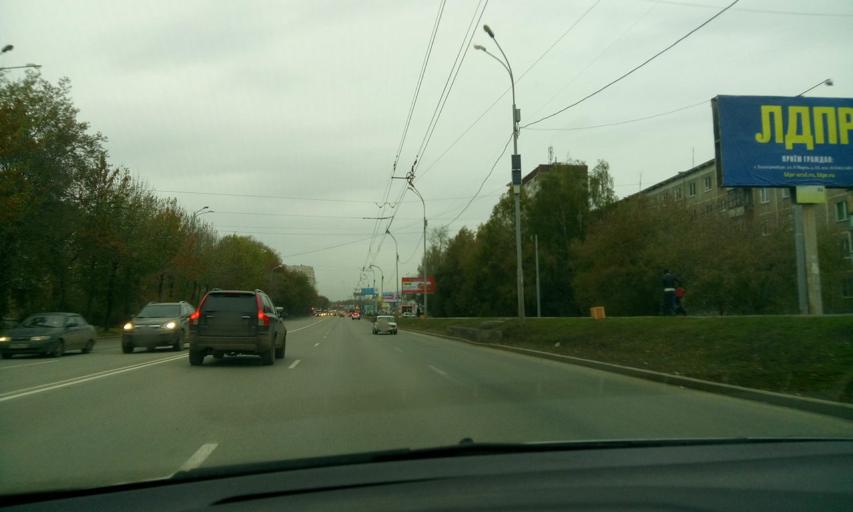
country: RU
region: Sverdlovsk
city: Yekaterinburg
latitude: 56.9079
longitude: 60.6133
